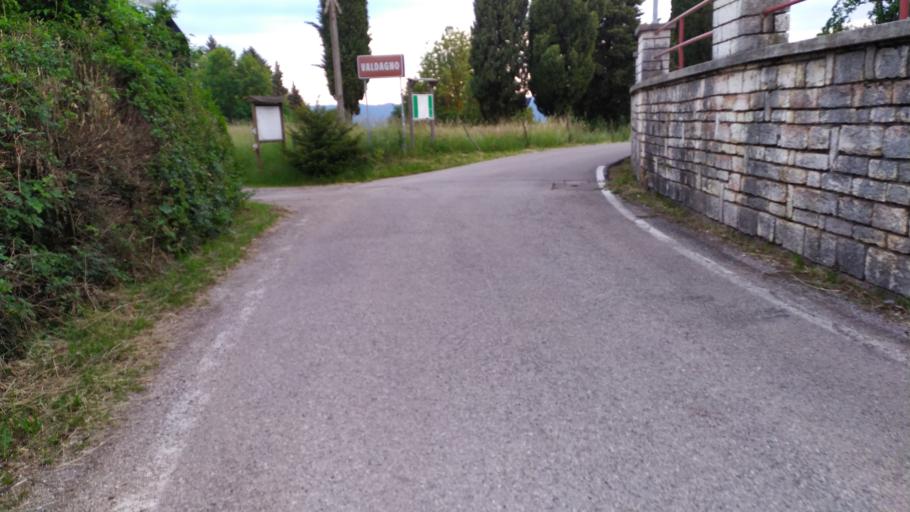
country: IT
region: Veneto
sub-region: Provincia di Vicenza
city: Monte di Malo
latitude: 45.6706
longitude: 11.3264
